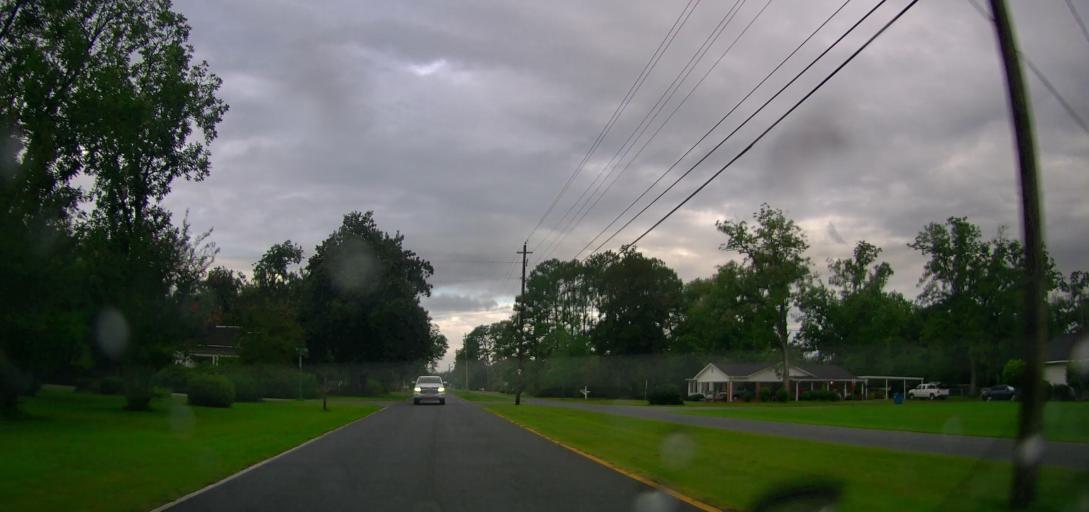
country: US
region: Georgia
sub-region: Ware County
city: Deenwood
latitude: 31.2299
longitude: -82.3853
